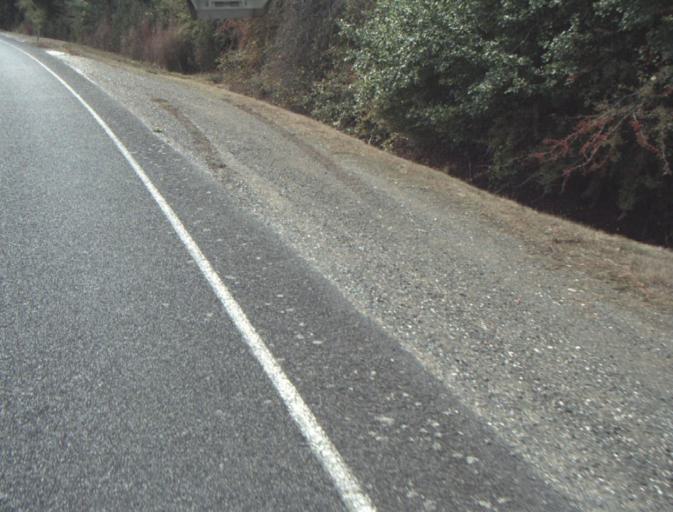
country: AU
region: Tasmania
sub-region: Launceston
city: Mayfield
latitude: -41.2788
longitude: 147.2202
